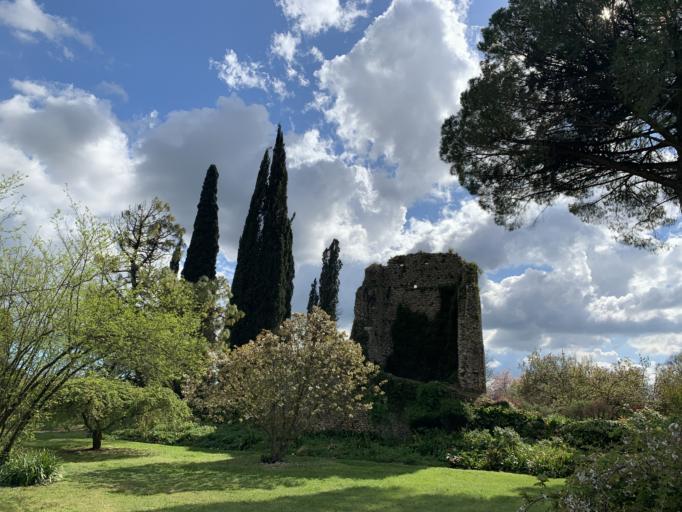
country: IT
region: Latium
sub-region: Provincia di Latina
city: Norma
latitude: 41.5809
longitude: 12.9521
